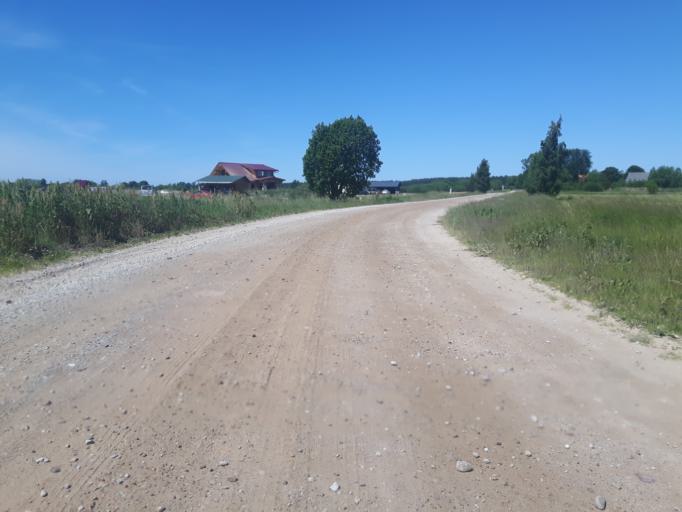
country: LV
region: Grobina
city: Grobina
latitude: 56.5292
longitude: 21.1307
